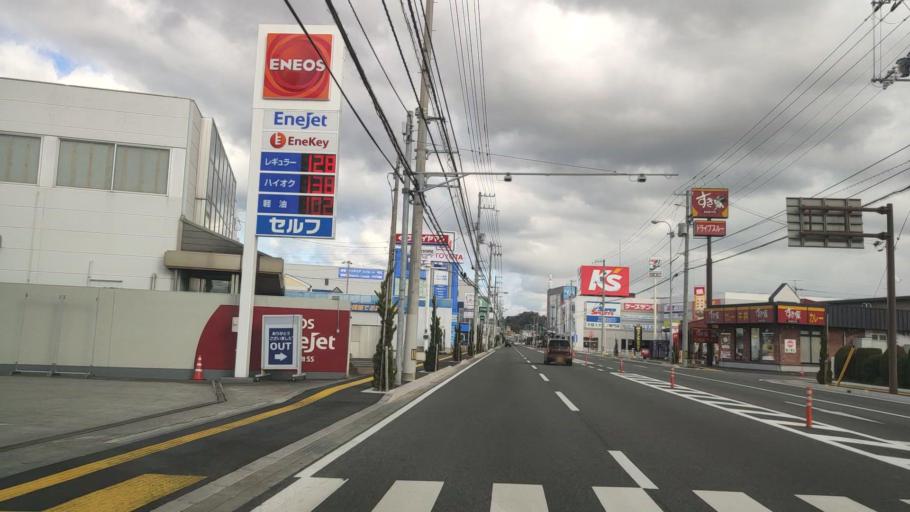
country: JP
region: Ehime
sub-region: Shikoku-chuo Shi
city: Matsuyama
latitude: 33.8631
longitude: 132.7500
